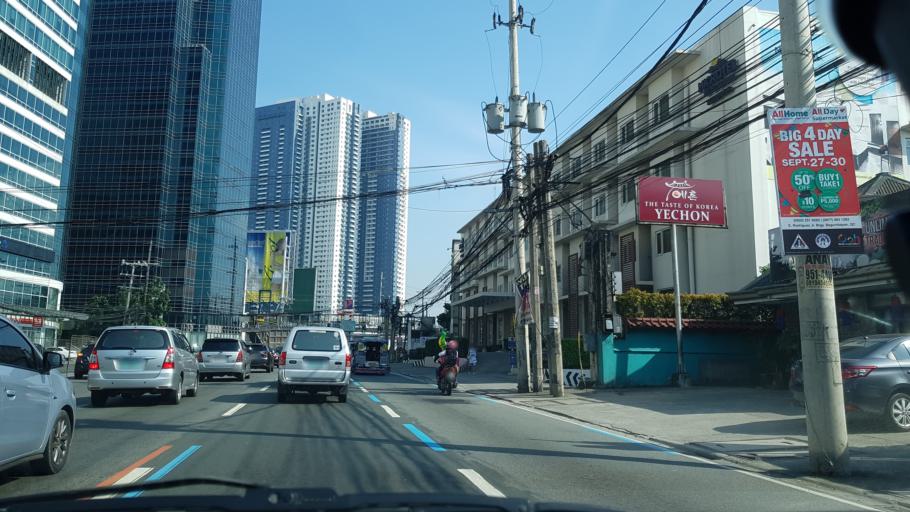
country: PH
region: Metro Manila
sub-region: Marikina
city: Calumpang
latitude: 14.6081
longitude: 121.0778
